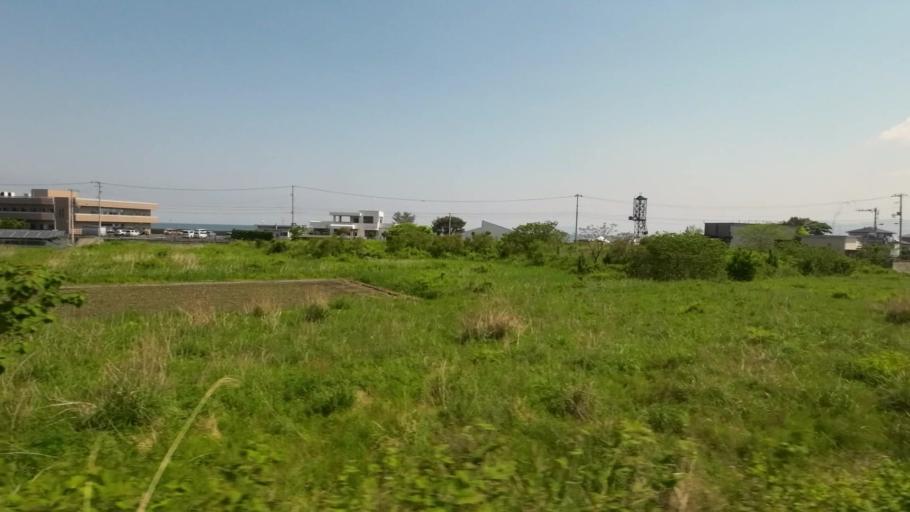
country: JP
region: Ehime
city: Kawanoecho
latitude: 33.9681
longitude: 133.4886
